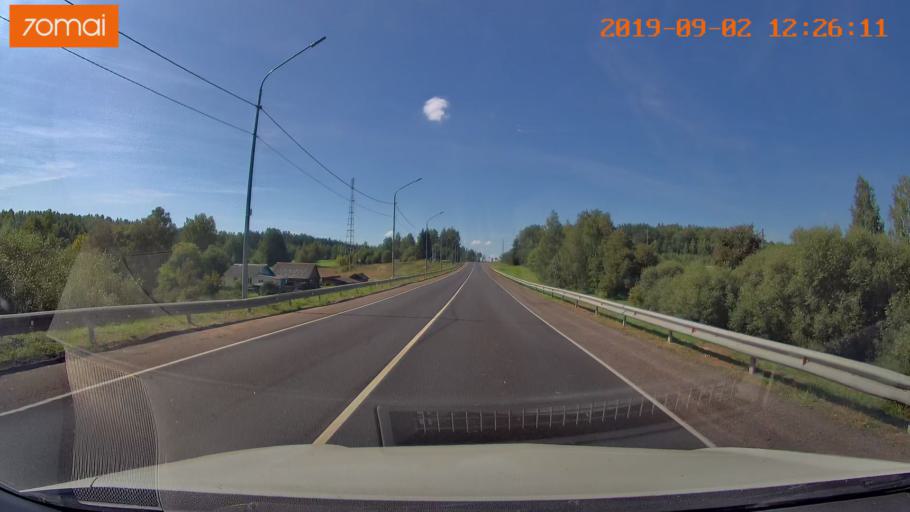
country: RU
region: Smolensk
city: Shumyachi
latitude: 53.8580
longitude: 32.5708
